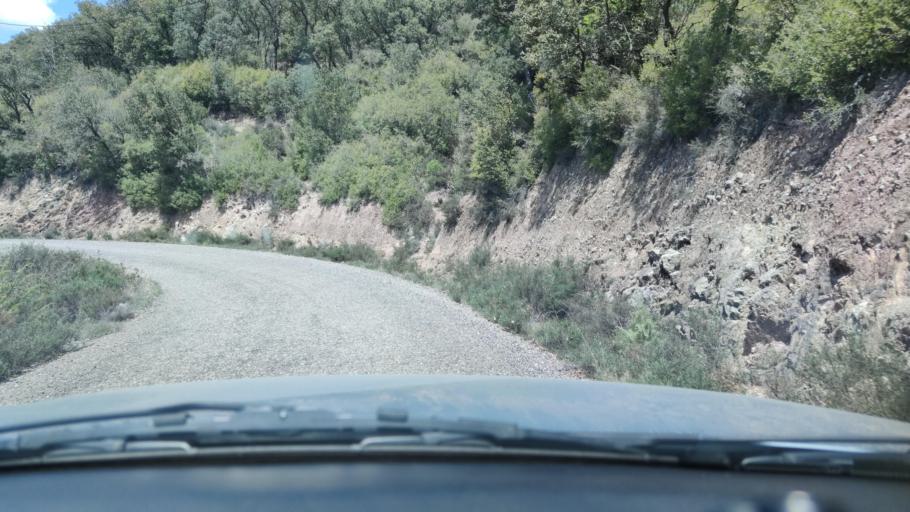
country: ES
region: Catalonia
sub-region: Provincia de Lleida
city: Sort
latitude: 42.3153
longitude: 1.0836
